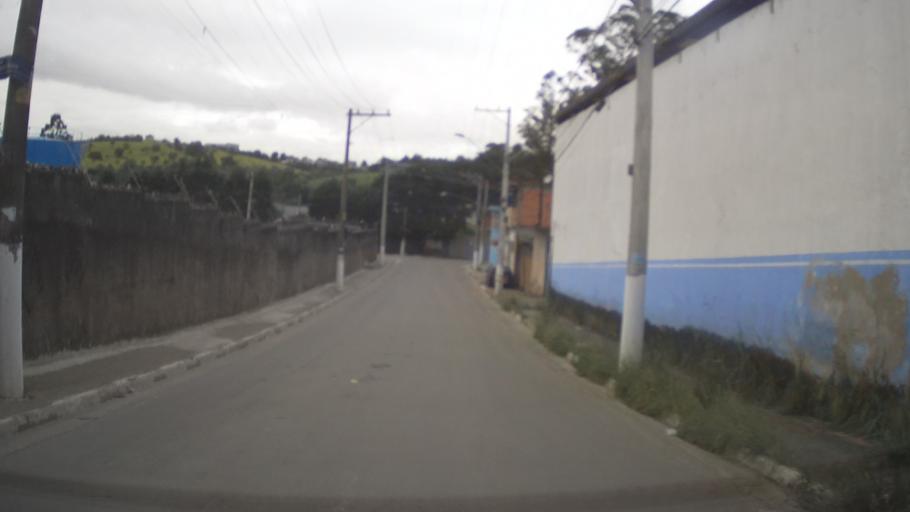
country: BR
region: Sao Paulo
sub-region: Itaquaquecetuba
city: Itaquaquecetuba
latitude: -23.4583
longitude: -46.3941
